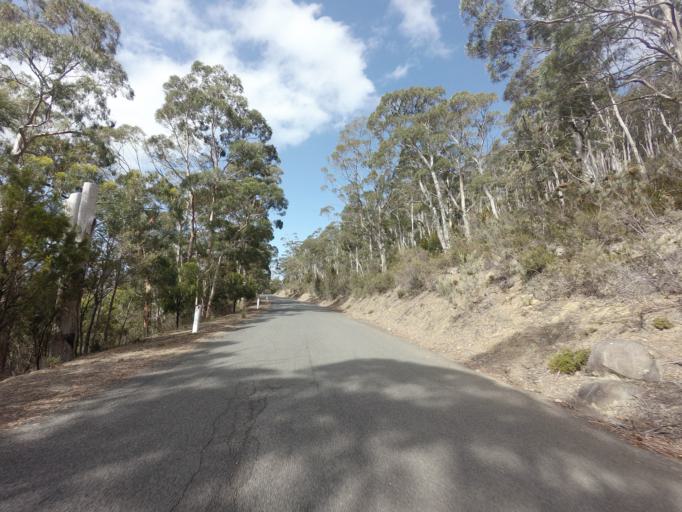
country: AU
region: Tasmania
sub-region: Hobart
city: Dynnyrne
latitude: -42.9163
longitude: 147.2773
